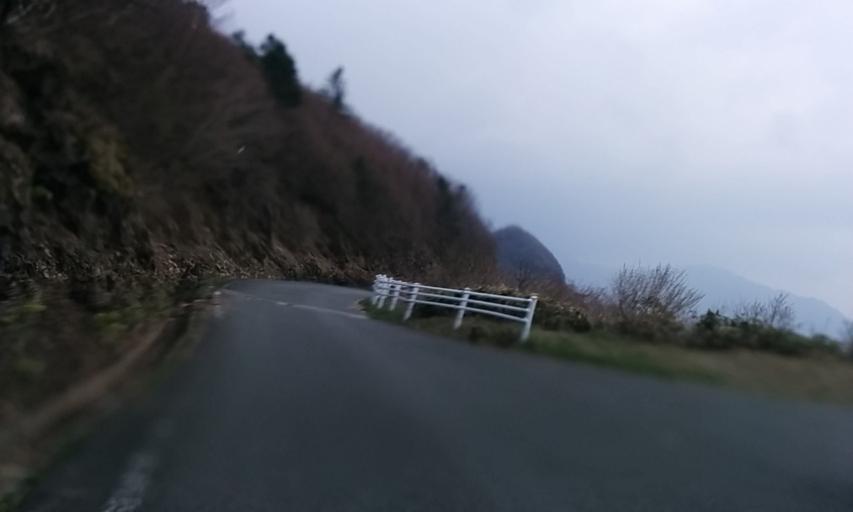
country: JP
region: Ehime
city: Saijo
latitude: 33.7841
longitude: 133.1900
